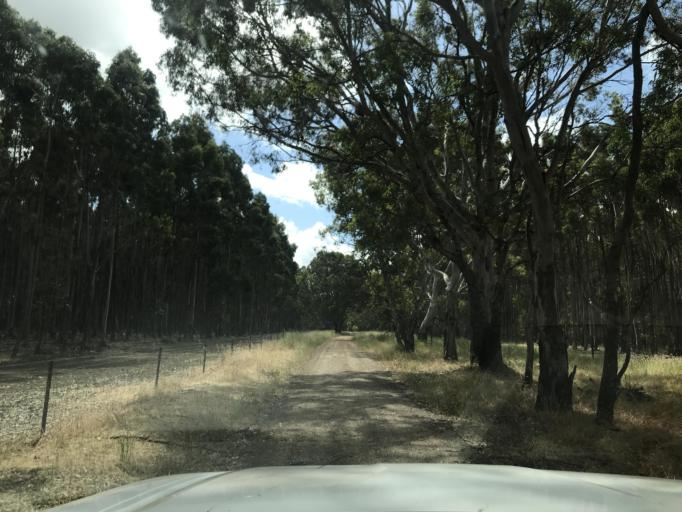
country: AU
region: South Australia
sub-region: Wattle Range
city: Penola
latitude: -37.1895
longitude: 141.3740
